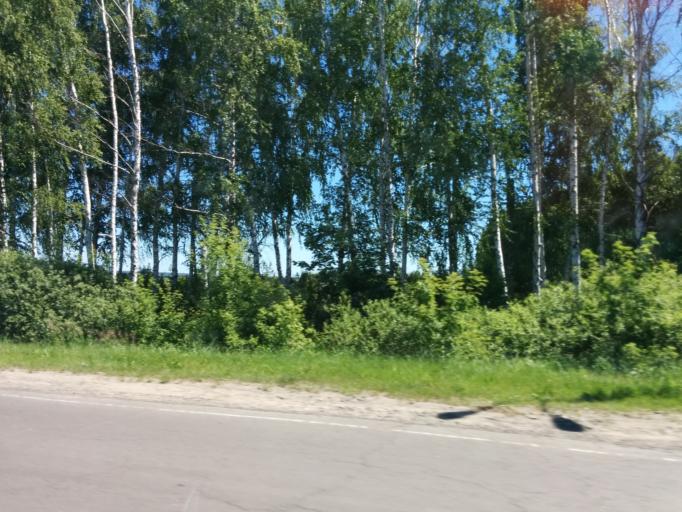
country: RU
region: Tambov
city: Goreloye
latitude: 53.1131
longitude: 41.5353
